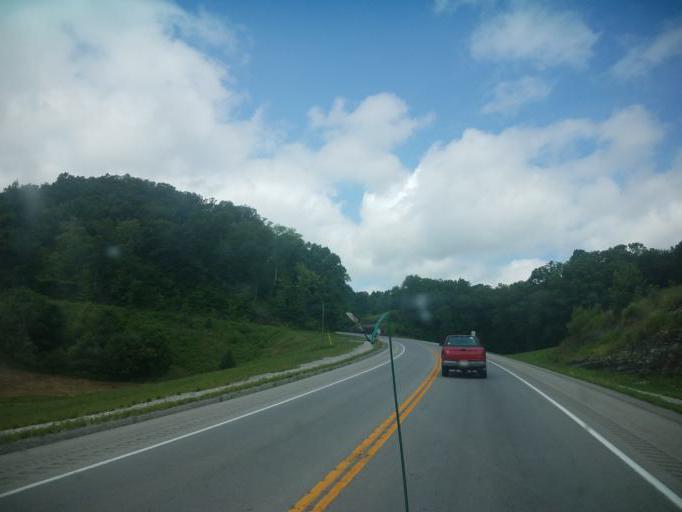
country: US
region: Kentucky
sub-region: Cumberland County
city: Burkesville
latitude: 36.8000
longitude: -85.3774
